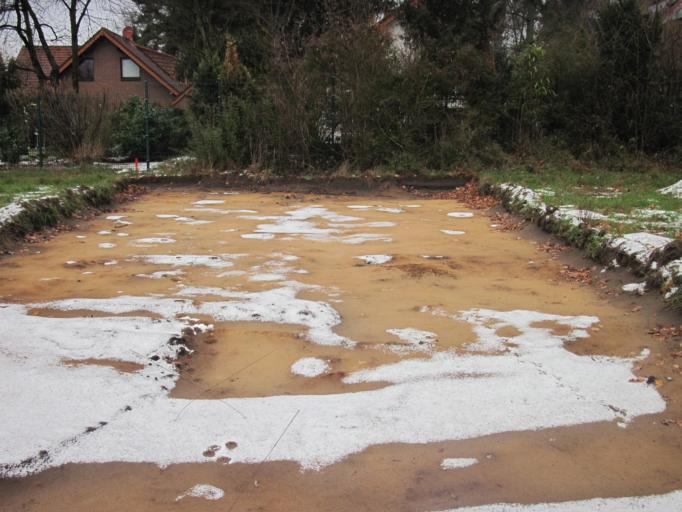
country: DE
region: North Rhine-Westphalia
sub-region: Regierungsbezirk Detmold
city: Paderborn
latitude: 51.7555
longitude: 8.7430
